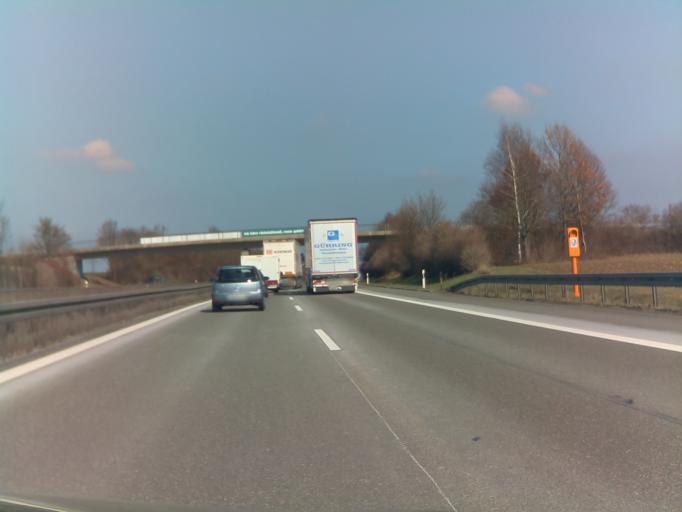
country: DE
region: Baden-Wuerttemberg
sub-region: Regierungsbezirk Stuttgart
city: Motzingen
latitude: 48.4714
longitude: 8.7888
